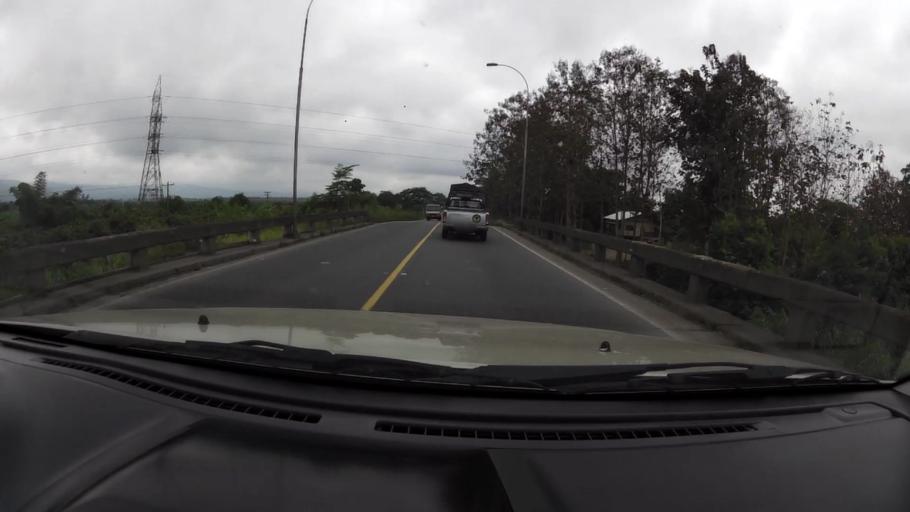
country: EC
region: Guayas
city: Balao
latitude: -2.8155
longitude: -79.7101
